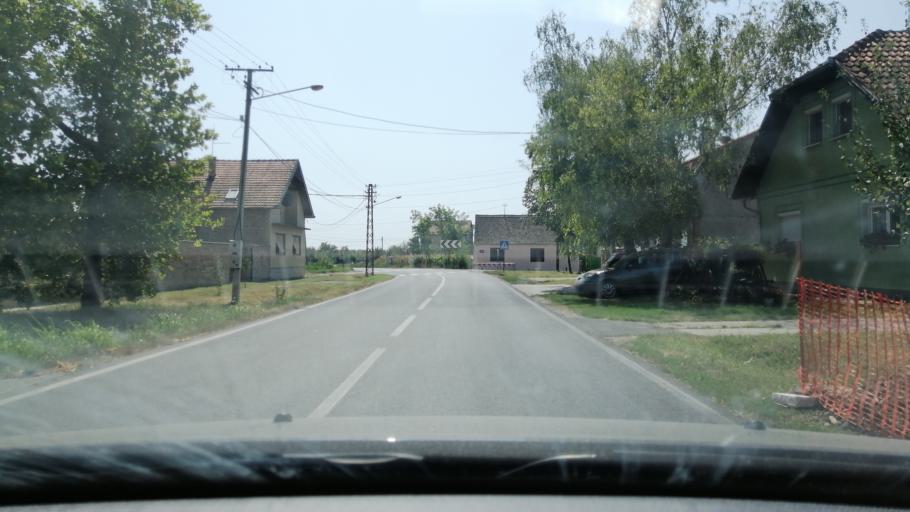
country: RS
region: Autonomna Pokrajina Vojvodina
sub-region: Juznobanatski Okrug
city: Pancevo
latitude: 44.7974
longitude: 20.7187
